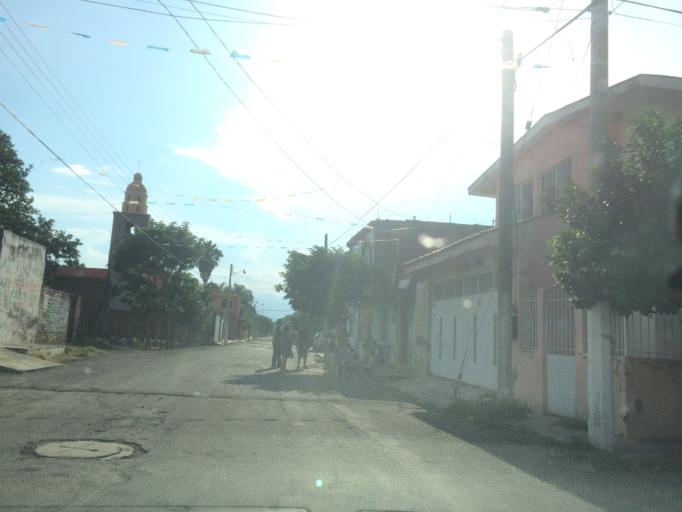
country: MX
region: Nayarit
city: Ixtlan del Rio
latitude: 21.0350
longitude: -104.3839
